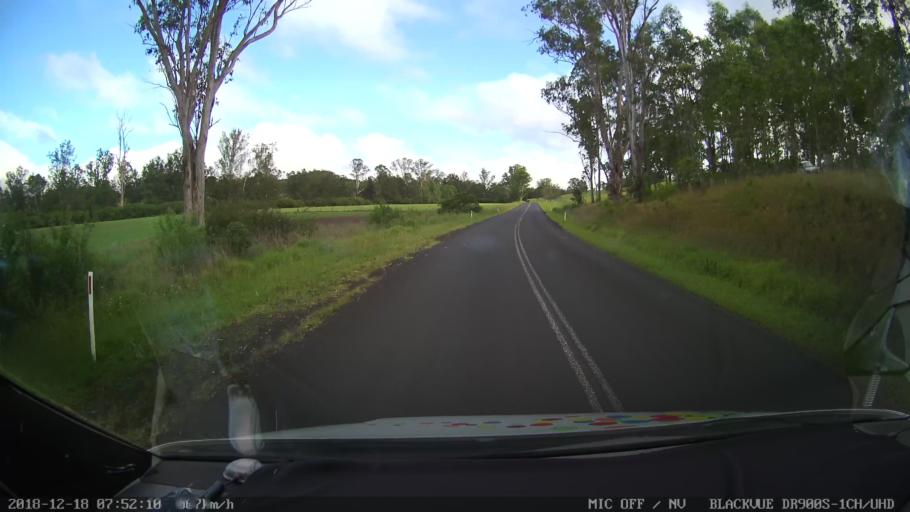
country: AU
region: New South Wales
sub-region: Kyogle
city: Kyogle
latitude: -28.4314
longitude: 152.5808
